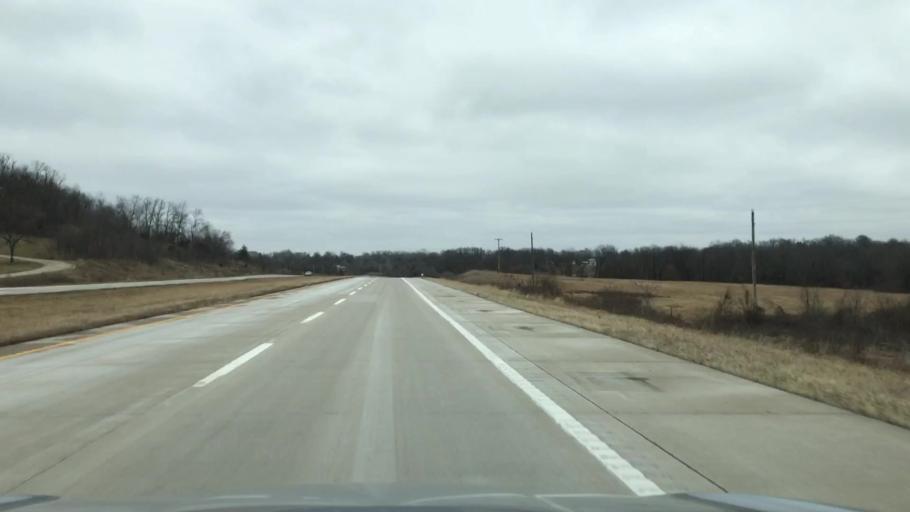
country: US
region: Missouri
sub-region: Livingston County
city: Chillicothe
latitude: 39.7400
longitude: -93.6457
